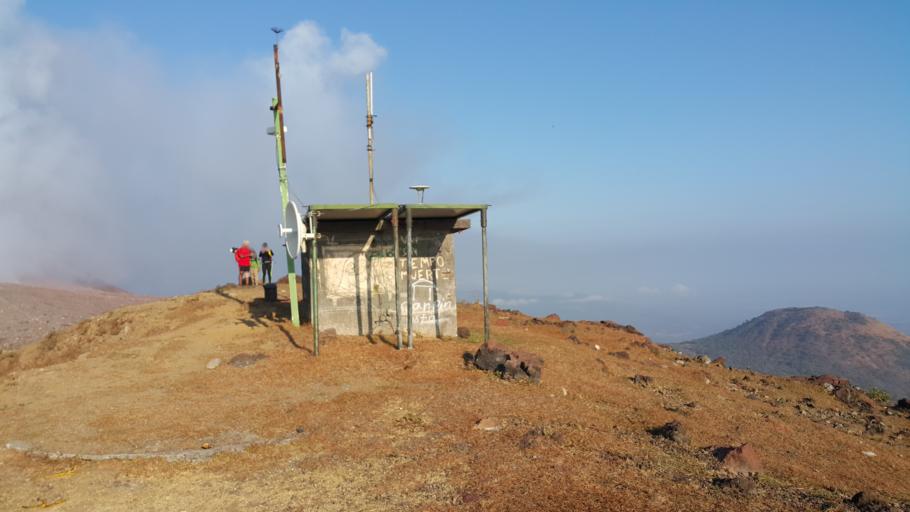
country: NI
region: Leon
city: Telica
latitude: 12.6063
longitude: -86.8347
